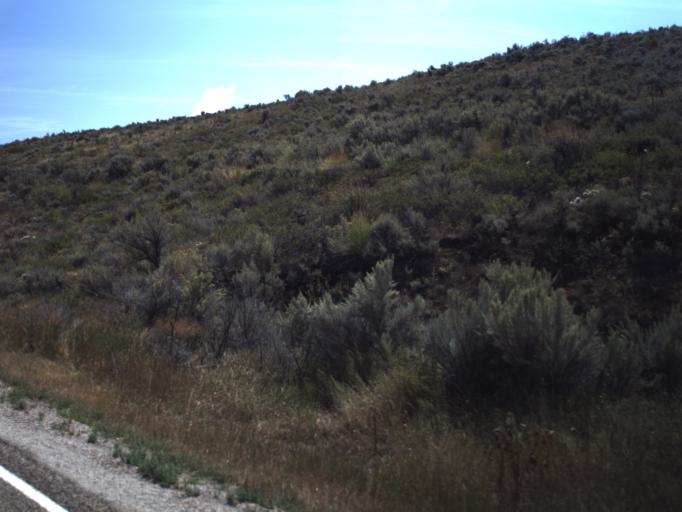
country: US
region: Utah
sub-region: Rich County
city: Randolph
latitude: 41.7824
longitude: -111.2025
